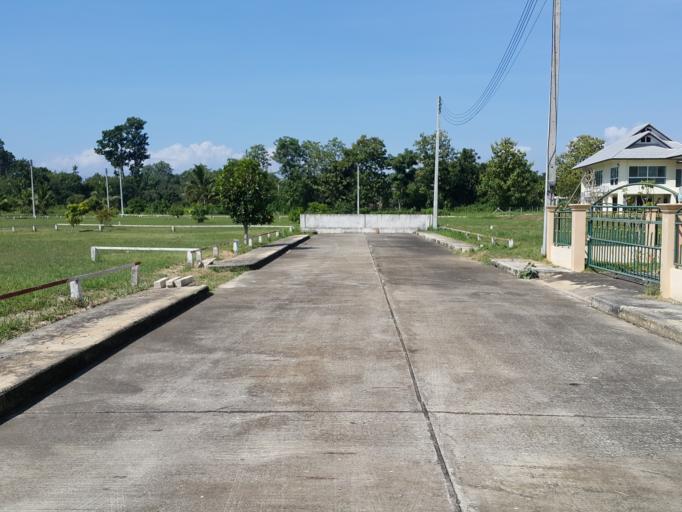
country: TH
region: Chiang Mai
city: San Sai
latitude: 18.8791
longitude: 99.1653
